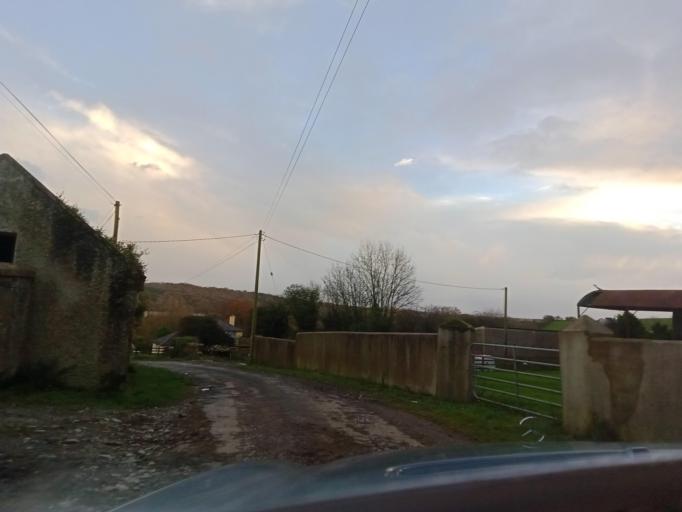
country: IE
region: Leinster
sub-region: Loch Garman
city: New Ross
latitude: 52.3454
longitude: -7.0033
